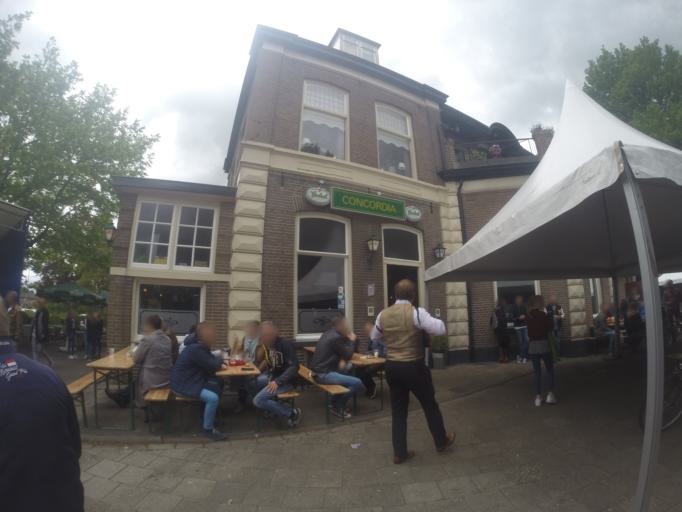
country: NL
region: Gelderland
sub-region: Gemeente Brummen
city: Brummen
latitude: 52.0880
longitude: 6.1523
